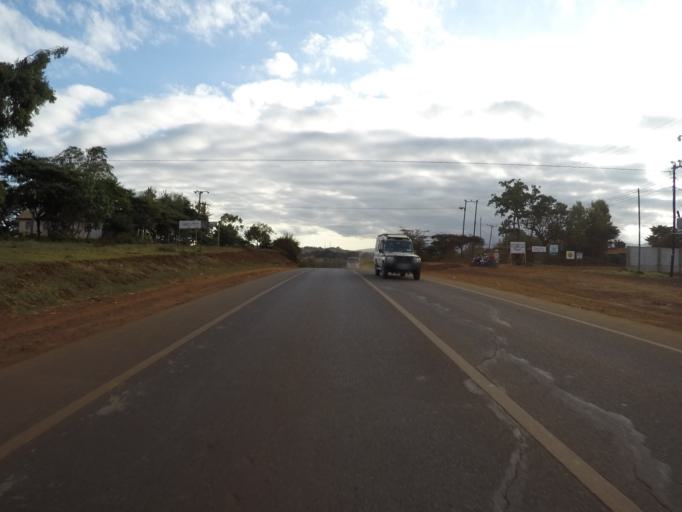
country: TZ
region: Arusha
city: Kiratu
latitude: -3.3378
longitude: 35.6895
